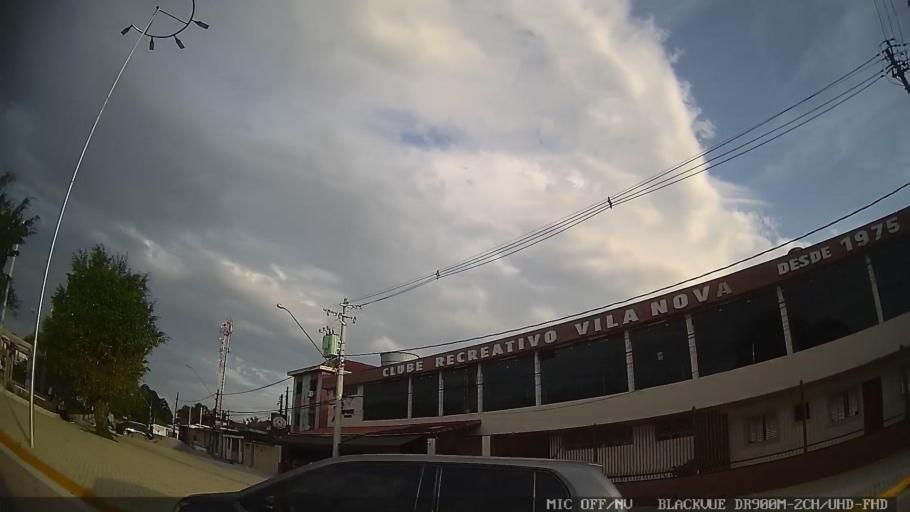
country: BR
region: Sao Paulo
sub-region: Cubatao
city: Cubatao
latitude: -23.8988
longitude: -46.4272
